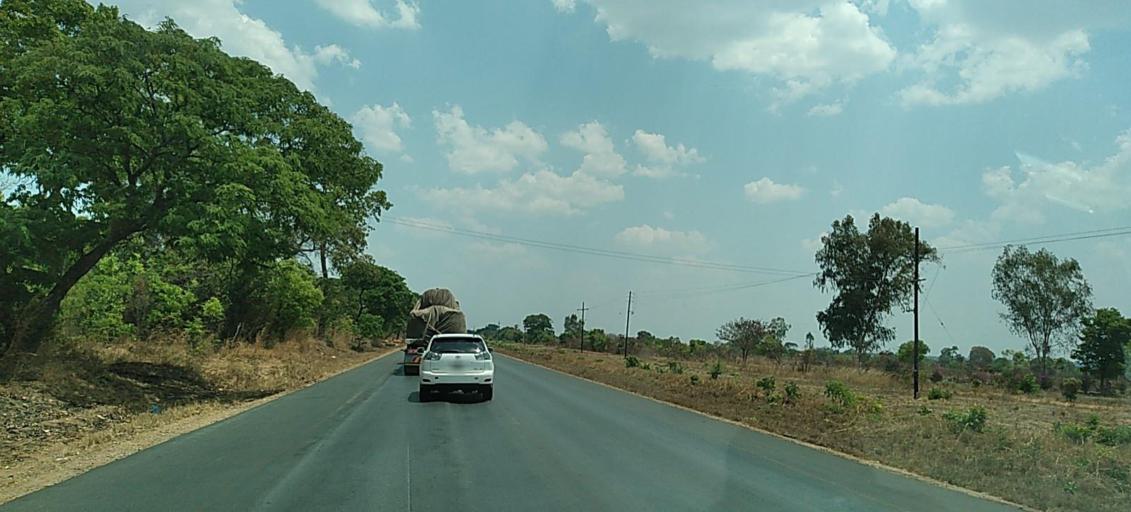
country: ZM
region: Central
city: Kabwe
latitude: -14.2669
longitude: 28.5551
